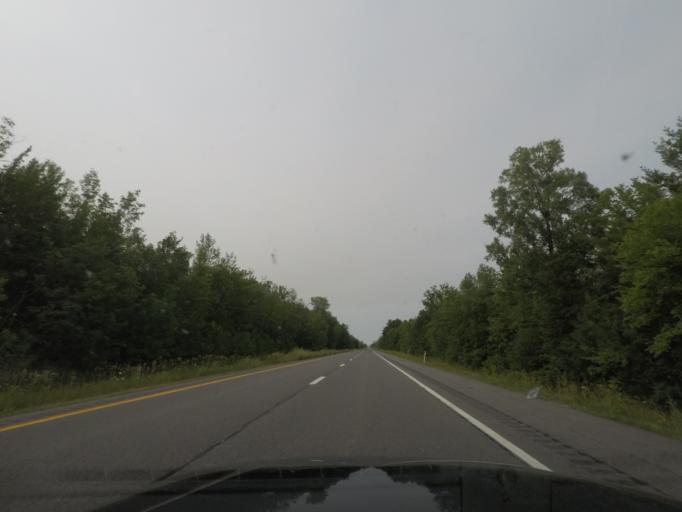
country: US
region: New York
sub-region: Clinton County
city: Champlain
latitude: 44.9333
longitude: -73.4465
